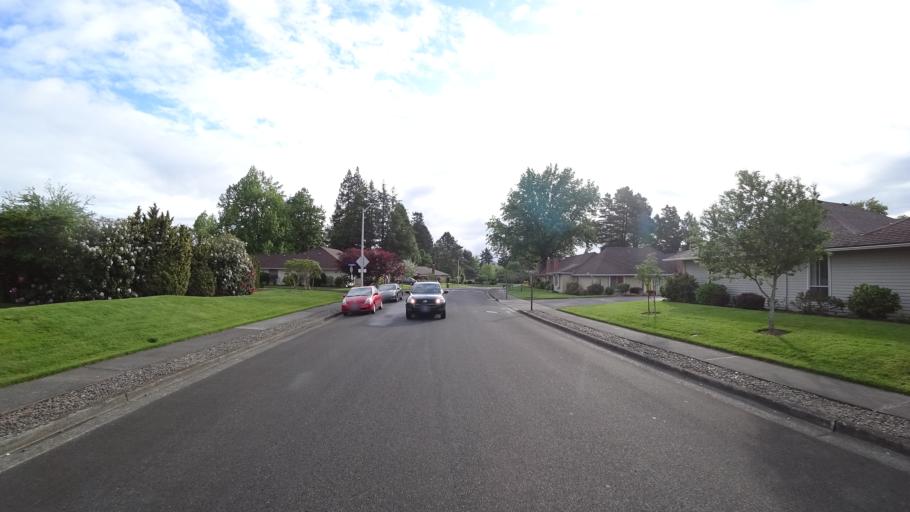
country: US
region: Oregon
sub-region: Washington County
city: Beaverton
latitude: 45.4824
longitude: -122.8233
